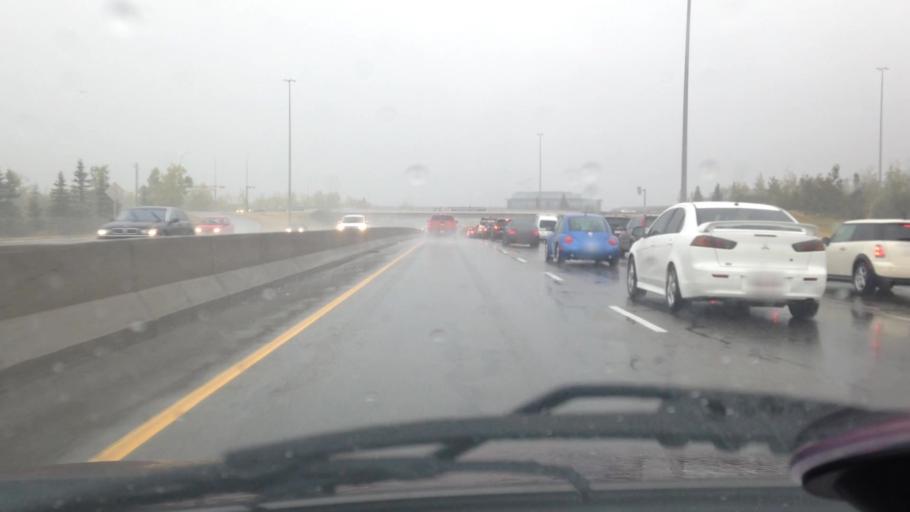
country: CA
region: Alberta
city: Calgary
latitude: 51.0111
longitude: -114.1180
